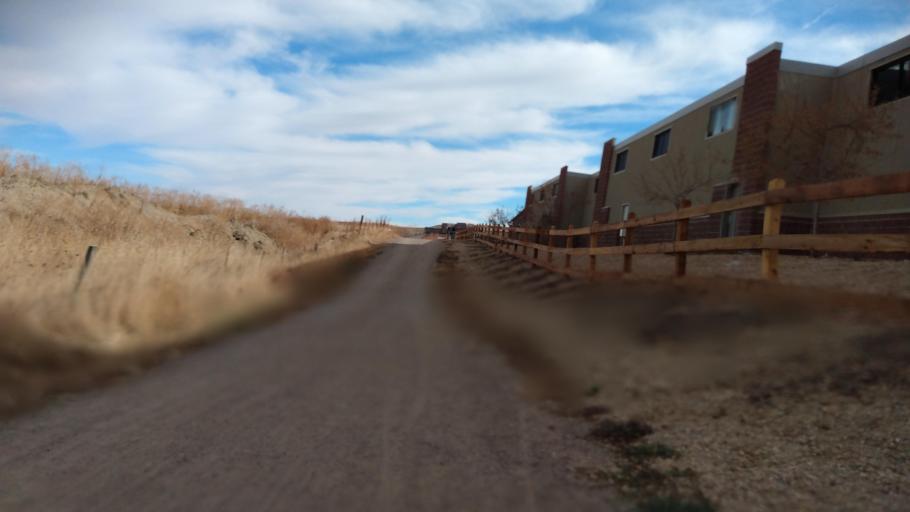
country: US
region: Colorado
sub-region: Boulder County
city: Lafayette
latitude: 39.9830
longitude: -105.0704
